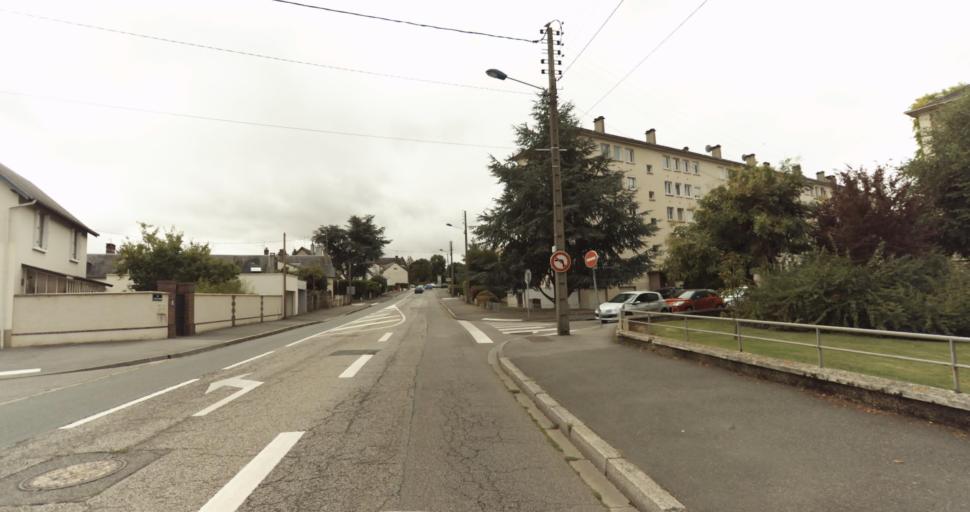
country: FR
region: Haute-Normandie
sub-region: Departement de l'Eure
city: Evreux
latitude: 49.0222
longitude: 1.1559
